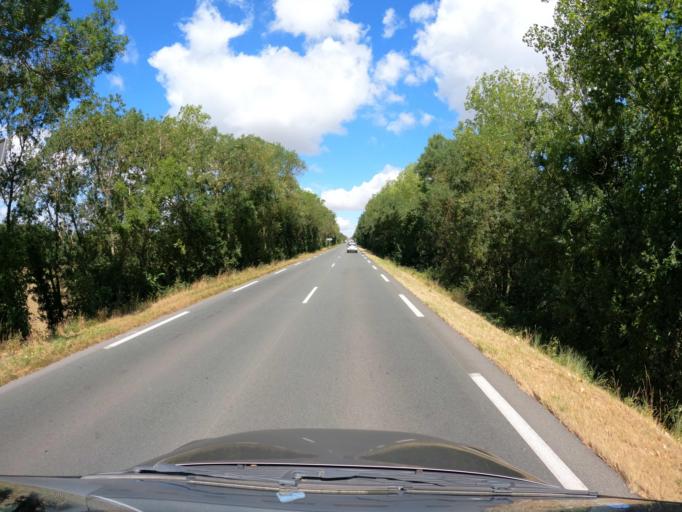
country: FR
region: Pays de la Loire
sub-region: Departement de Maine-et-Loire
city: Lire
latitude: 47.3529
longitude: -1.1699
